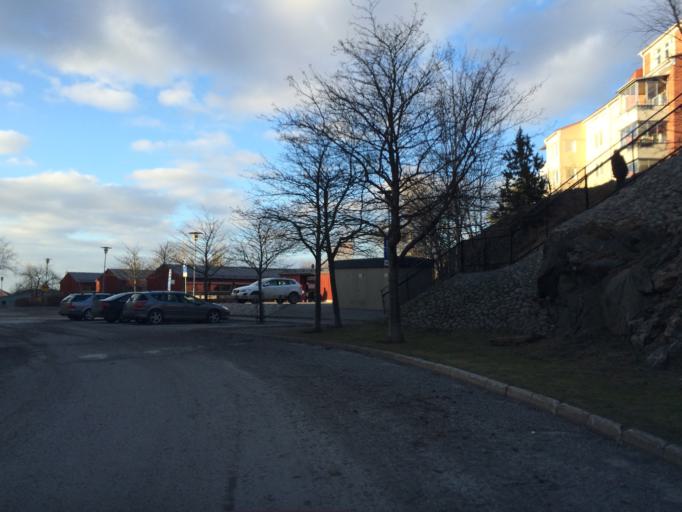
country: SE
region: Stockholm
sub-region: Nacka Kommun
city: Nacka
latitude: 59.3161
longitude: 18.1648
